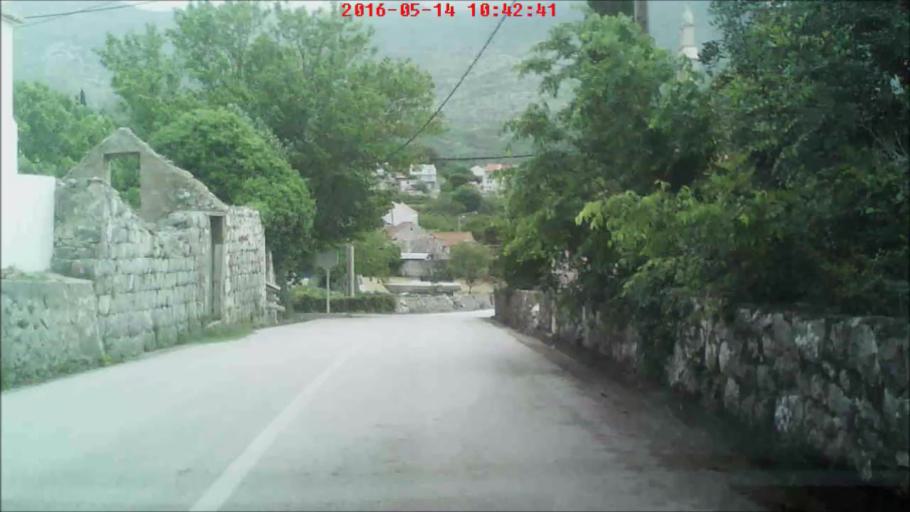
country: HR
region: Dubrovacko-Neretvanska
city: Podgora
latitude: 42.7841
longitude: 17.8761
